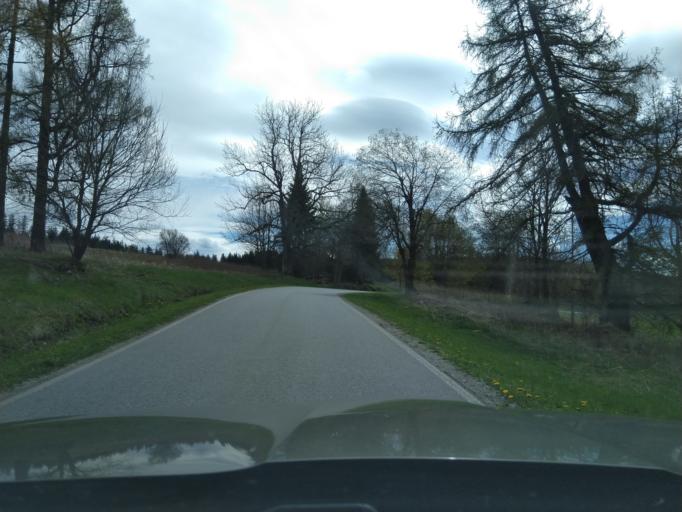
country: CZ
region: Jihocesky
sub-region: Okres Prachatice
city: Zdikov
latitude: 49.0412
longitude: 13.6686
